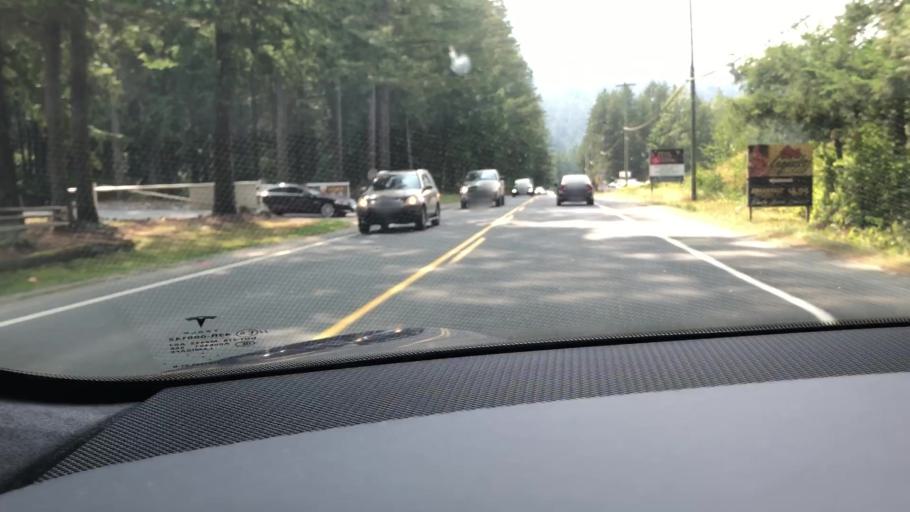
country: CA
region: British Columbia
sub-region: Fraser Valley Regional District
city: Chilliwack
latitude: 49.0751
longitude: -121.9673
